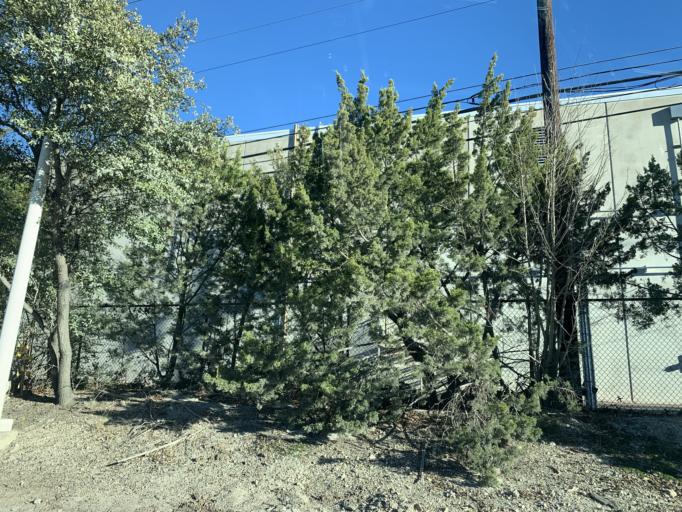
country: US
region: Texas
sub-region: Travis County
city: Wells Branch
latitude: 30.4000
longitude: -97.7099
